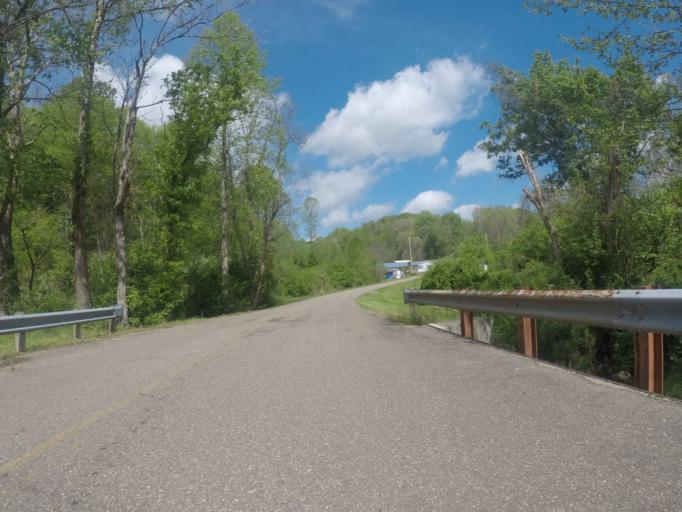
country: US
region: West Virginia
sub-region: Cabell County
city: Huntington
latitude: 38.5177
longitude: -82.4397
